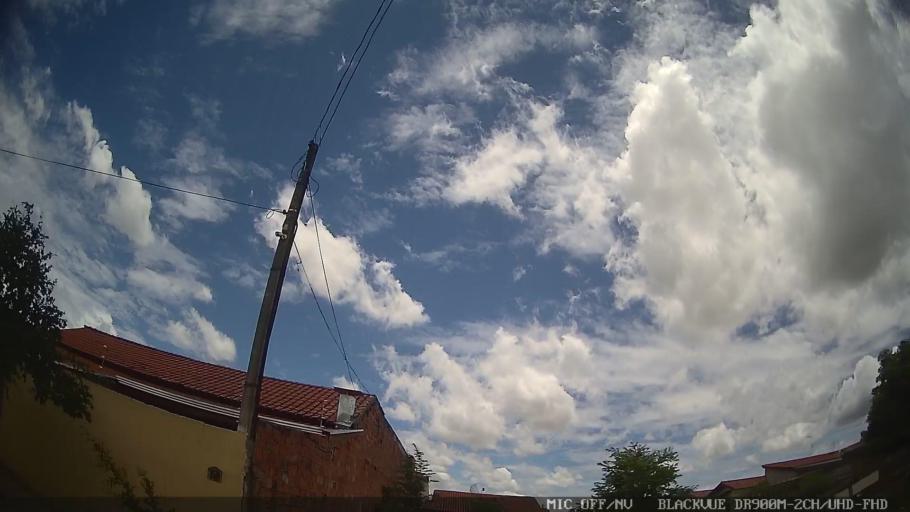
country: BR
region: Sao Paulo
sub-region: Jaguariuna
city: Jaguariuna
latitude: -22.6946
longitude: -47.0010
